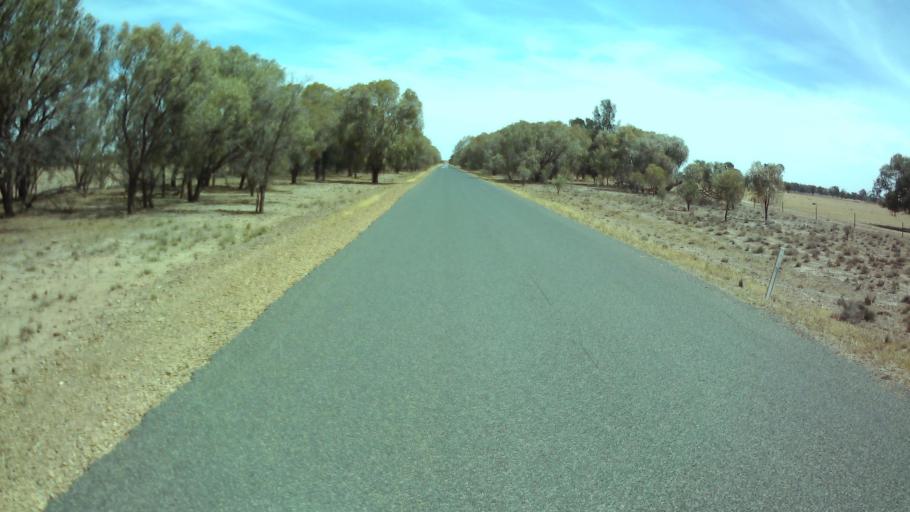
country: AU
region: New South Wales
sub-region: Weddin
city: Grenfell
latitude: -33.8725
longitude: 147.7444
